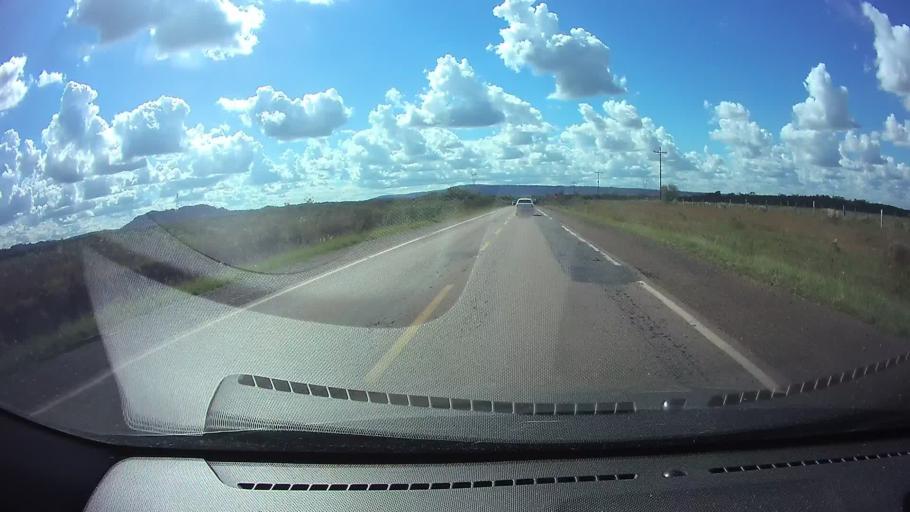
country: PY
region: Paraguari
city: Sapucai
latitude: -25.7320
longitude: -56.8197
